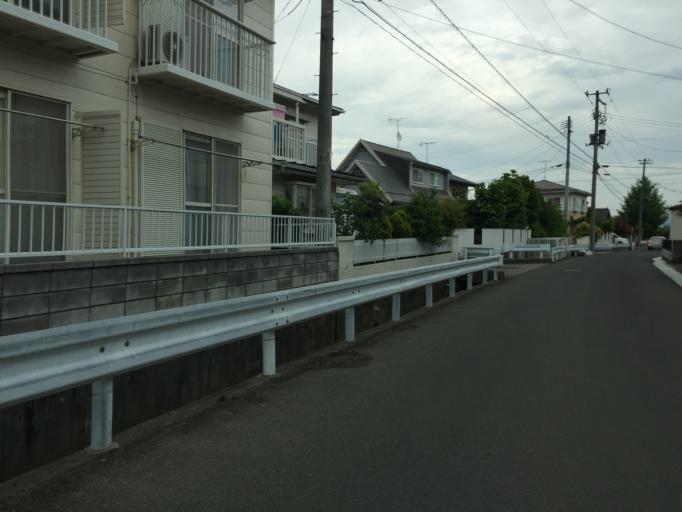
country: JP
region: Fukushima
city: Fukushima-shi
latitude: 37.7969
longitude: 140.4427
